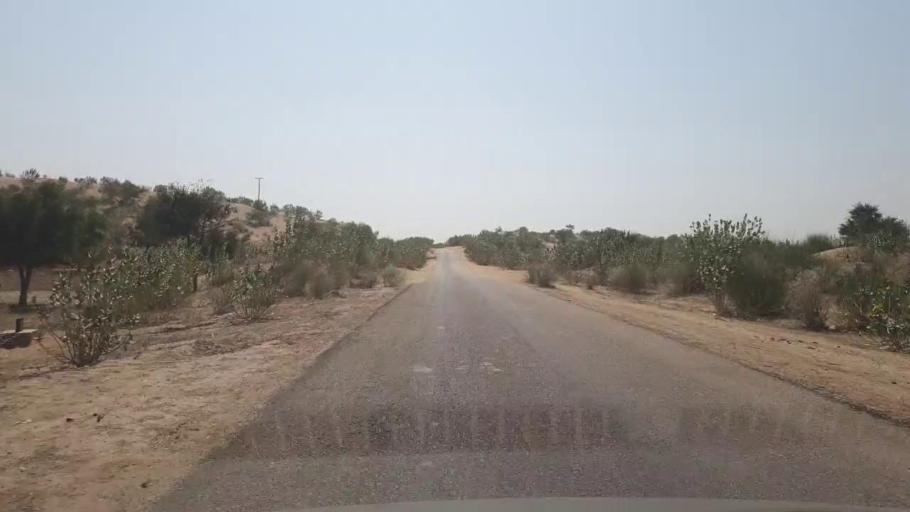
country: PK
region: Sindh
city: Chor
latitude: 25.6546
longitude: 70.1673
